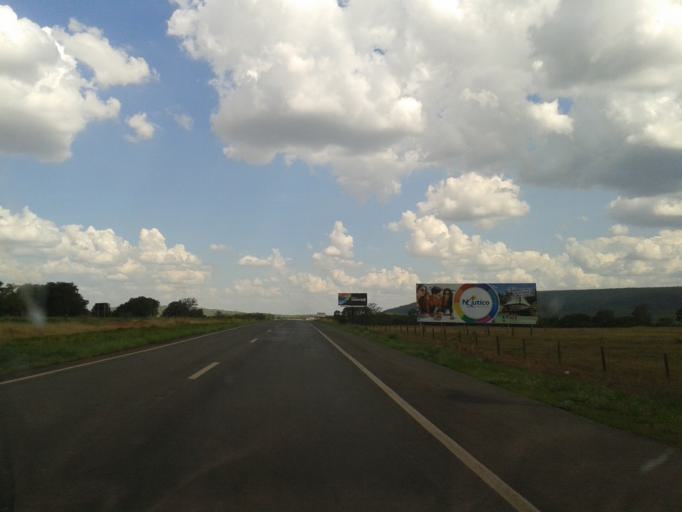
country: BR
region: Goias
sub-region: Caldas Novas
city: Caldas Novas
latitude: -17.7023
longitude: -48.7063
